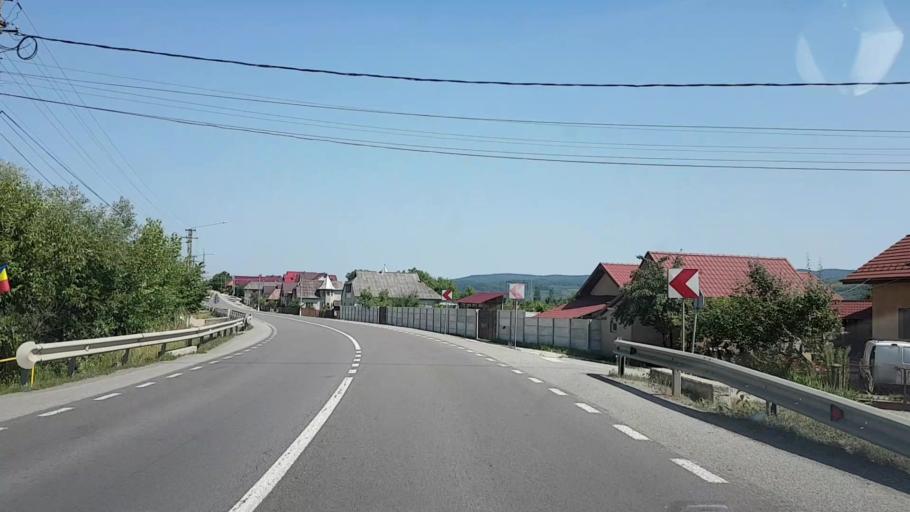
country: RO
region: Bistrita-Nasaud
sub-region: Comuna Uriu
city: Cristestii Ciceului
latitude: 47.1915
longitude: 24.0977
